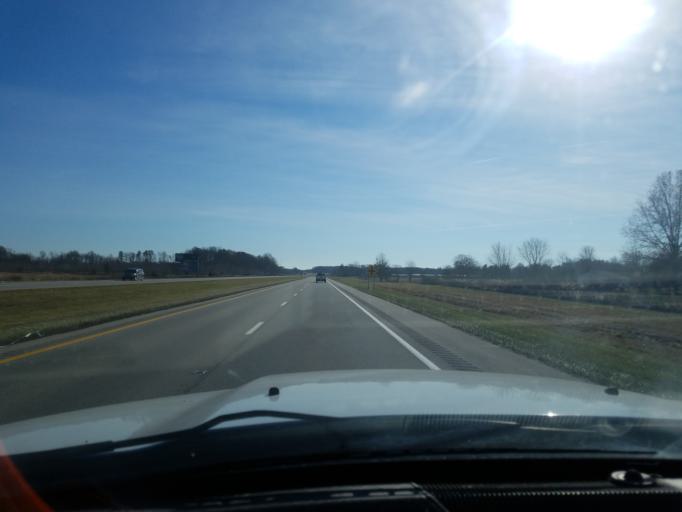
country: US
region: Ohio
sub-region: Adams County
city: Winchester
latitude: 38.9839
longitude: -83.7546
